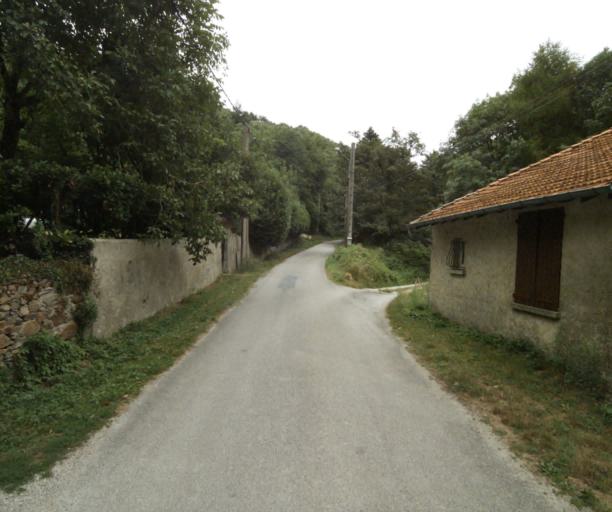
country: FR
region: Midi-Pyrenees
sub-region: Departement du Tarn
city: Soreze
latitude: 43.4367
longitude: 2.0716
